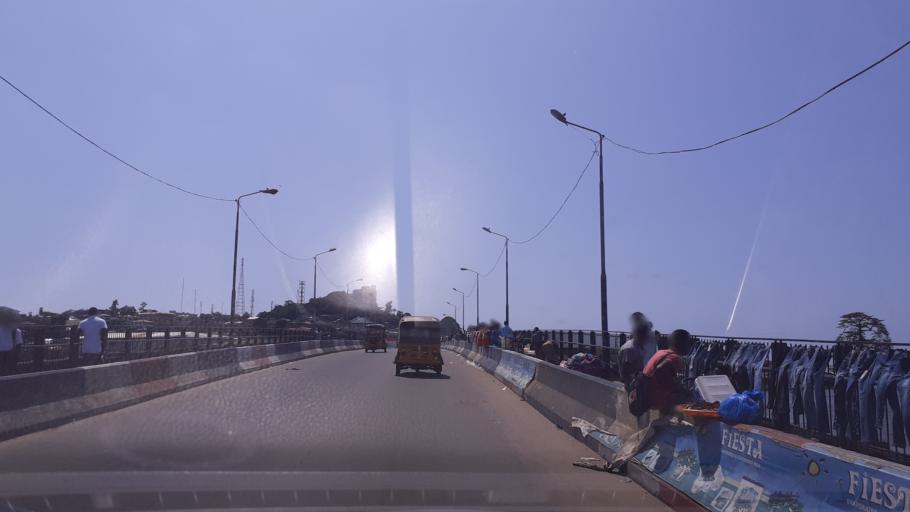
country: LR
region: Montserrado
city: Monrovia
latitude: 6.3226
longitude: -10.8041
